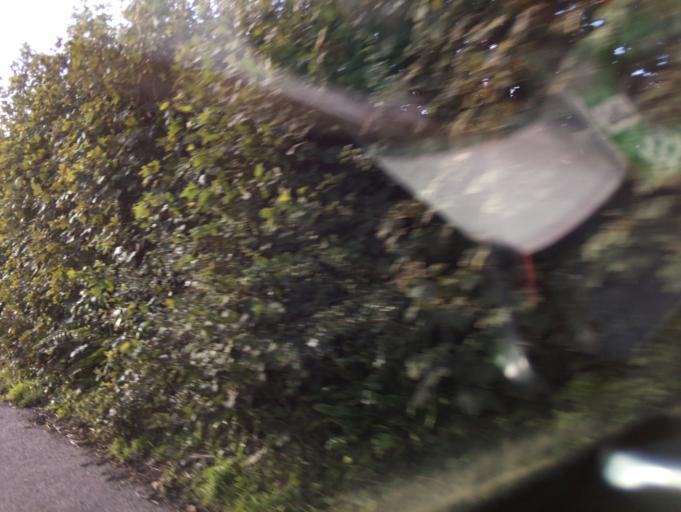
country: GB
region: England
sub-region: Devon
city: Totnes
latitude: 50.3461
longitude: -3.6762
